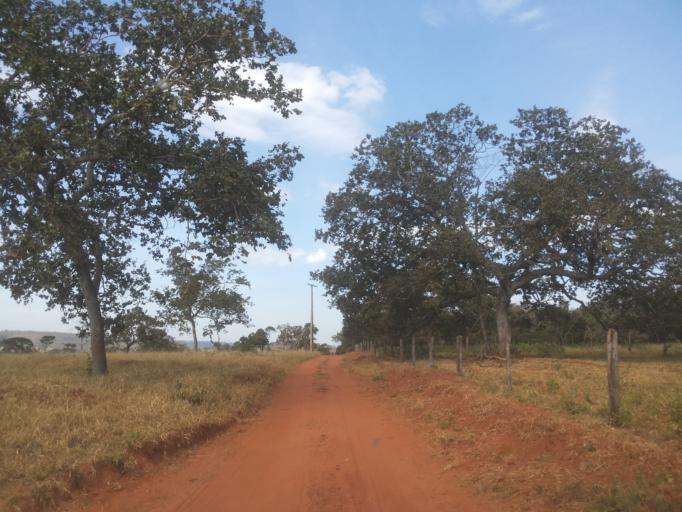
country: BR
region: Minas Gerais
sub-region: Ituiutaba
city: Ituiutaba
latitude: -19.0705
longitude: -49.3641
